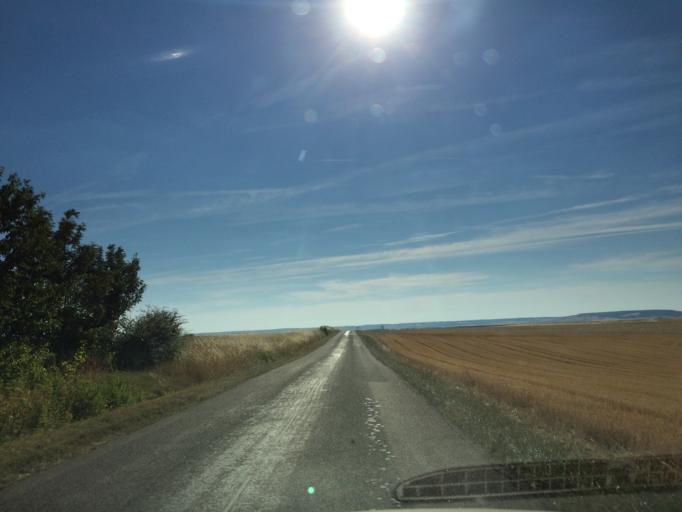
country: FR
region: Bourgogne
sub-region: Departement de l'Yonne
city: Laroche-Saint-Cydroine
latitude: 47.9203
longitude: 3.4932
